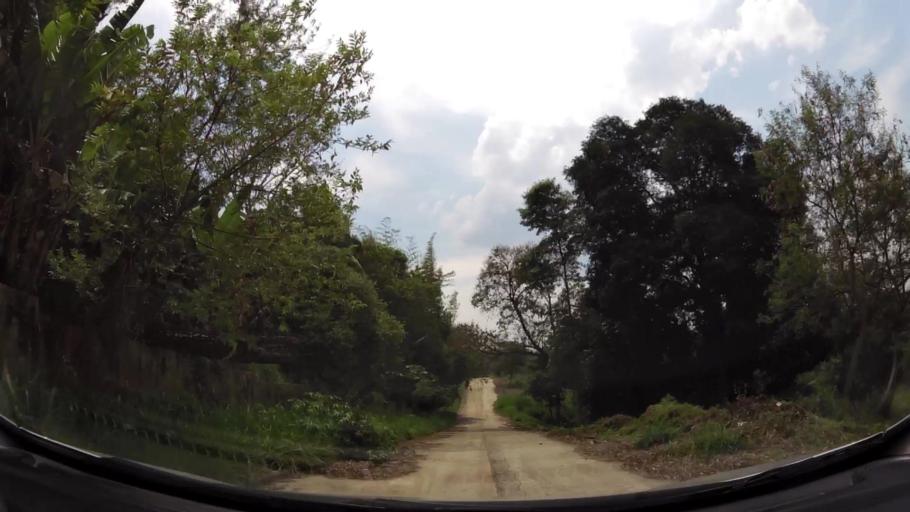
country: PY
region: Alto Parana
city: Ciudad del Este
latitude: -25.4891
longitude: -54.6073
